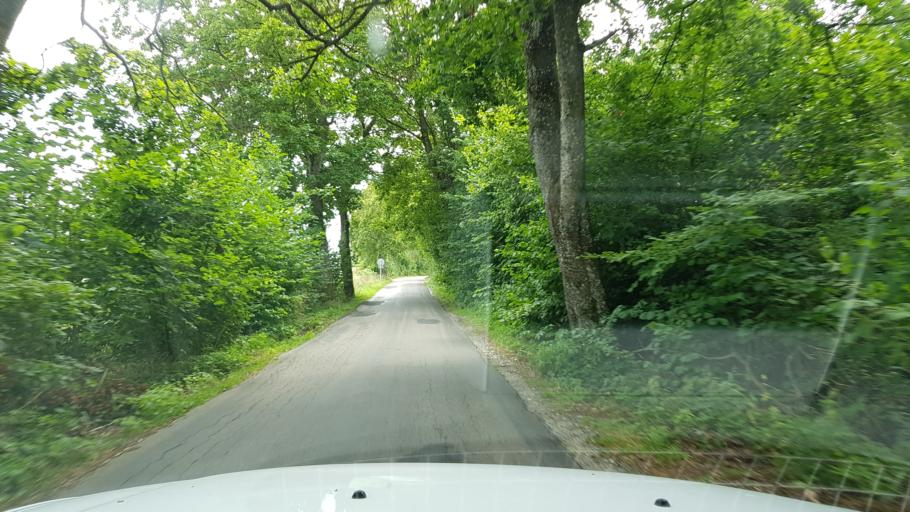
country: PL
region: West Pomeranian Voivodeship
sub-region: Koszalin
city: Koszalin
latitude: 54.1577
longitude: 16.0759
